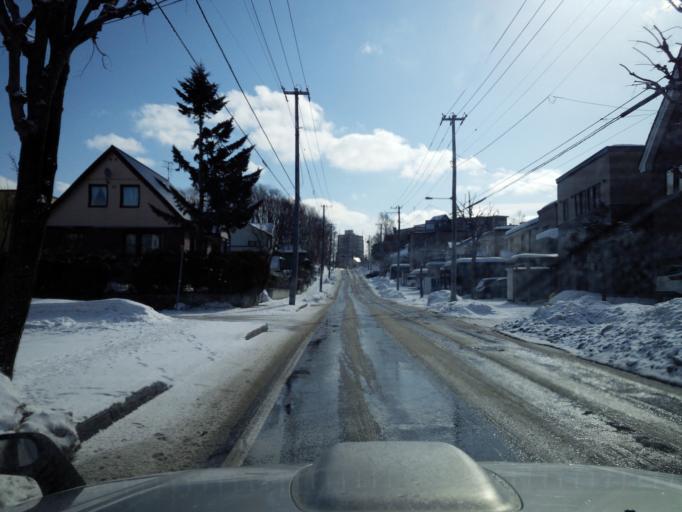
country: JP
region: Hokkaido
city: Sapporo
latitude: 42.9871
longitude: 141.4415
